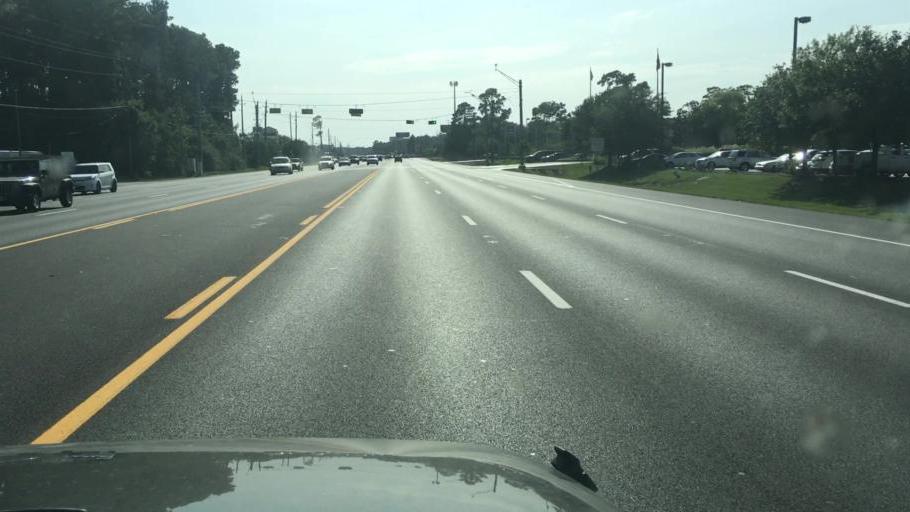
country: US
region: Texas
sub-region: Harris County
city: Humble
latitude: 30.0050
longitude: -95.2899
